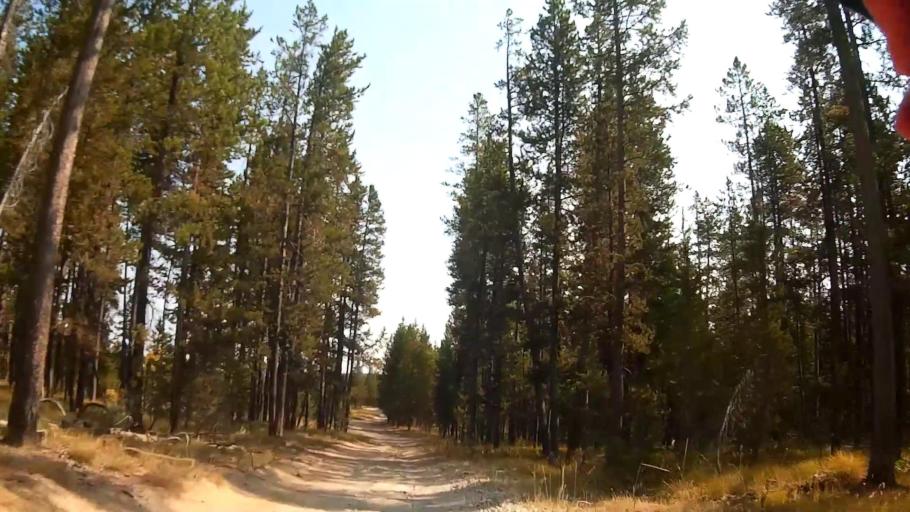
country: US
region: Montana
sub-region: Gallatin County
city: West Yellowstone
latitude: 44.5711
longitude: -111.1889
